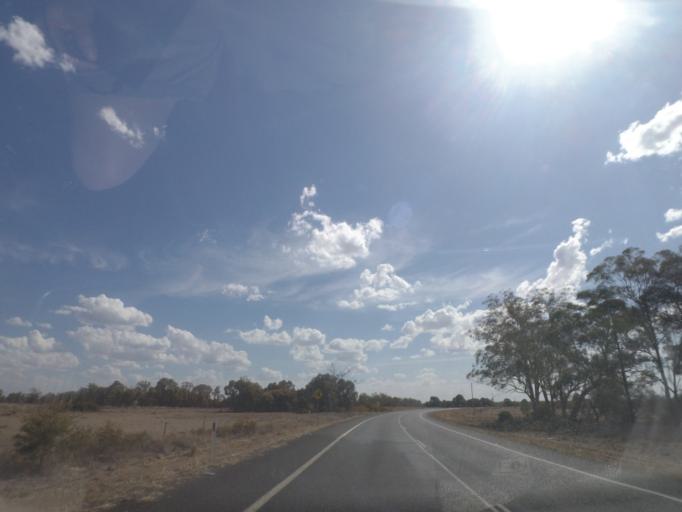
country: AU
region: Queensland
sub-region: Southern Downs
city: Stanthorpe
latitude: -28.4131
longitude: 151.1652
